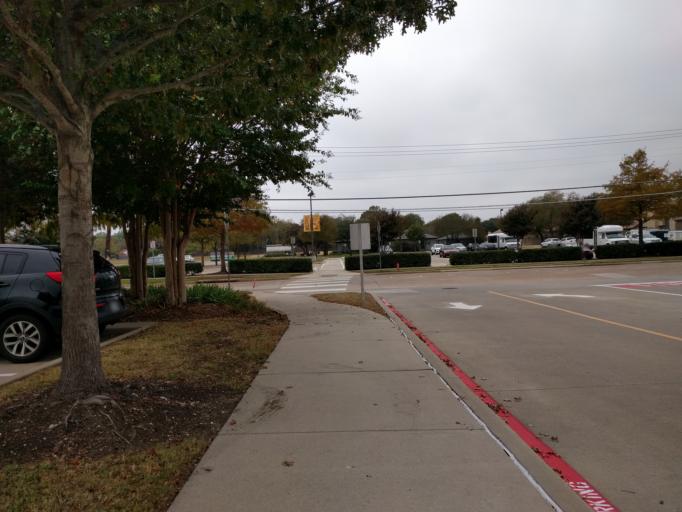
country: US
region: Texas
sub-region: Dallas County
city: Richardson
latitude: 32.9565
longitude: -96.7349
